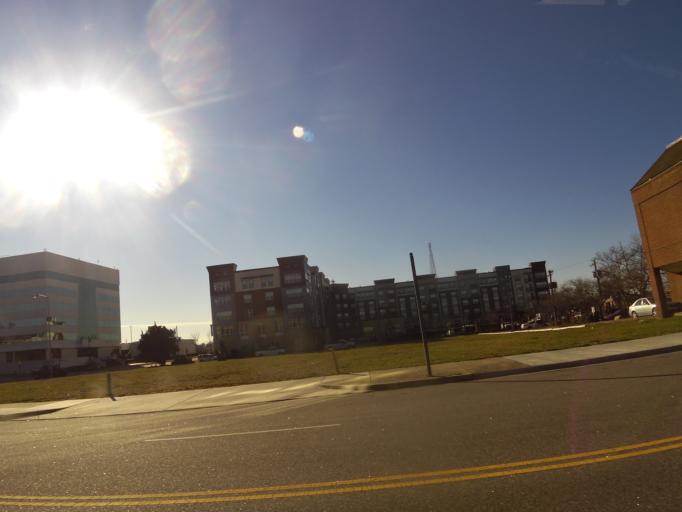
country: US
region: Virginia
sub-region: City of Portsmouth
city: Portsmouth
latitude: 36.8339
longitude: -76.2983
